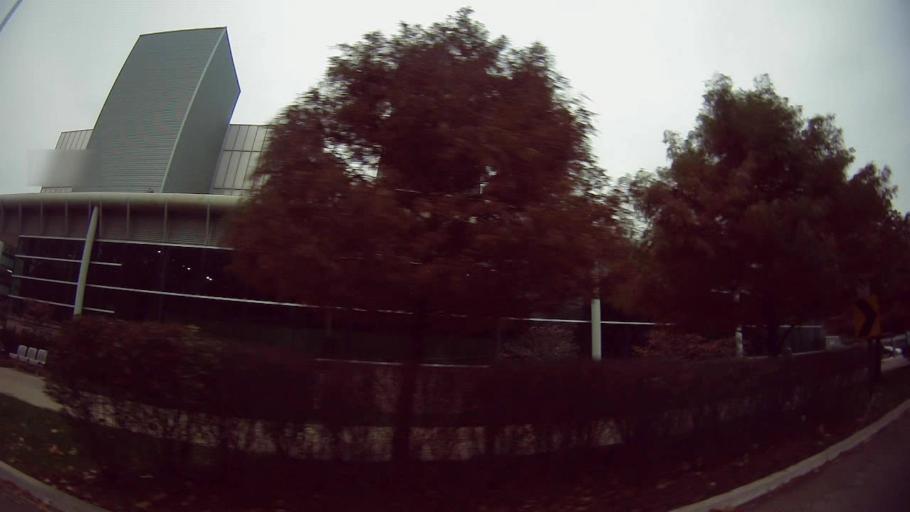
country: US
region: Michigan
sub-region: Wayne County
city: Detroit
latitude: 42.3582
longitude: -83.0626
